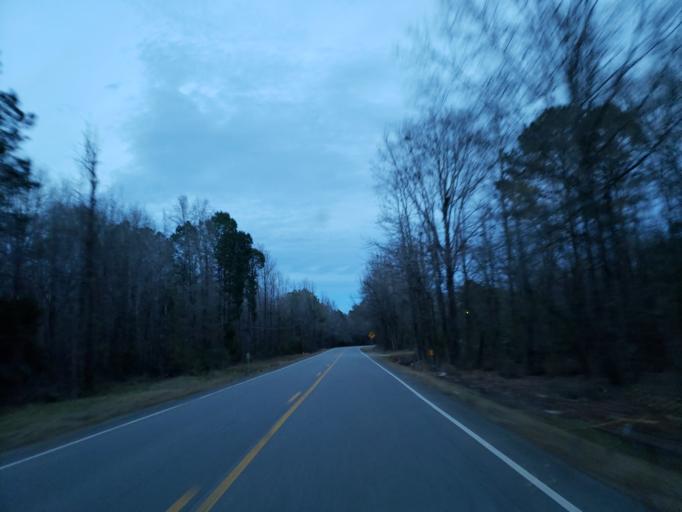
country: US
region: Alabama
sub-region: Greene County
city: Eutaw
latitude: 32.8517
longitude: -88.1124
